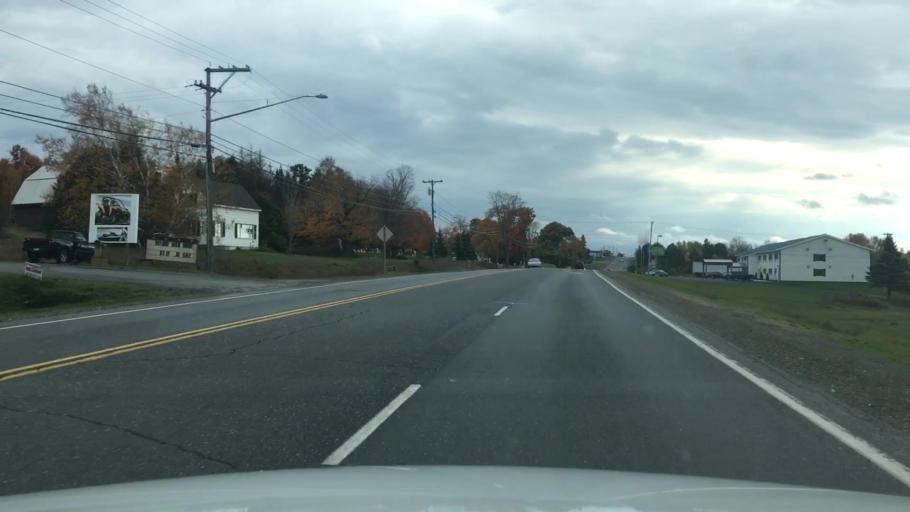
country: US
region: Maine
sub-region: Aroostook County
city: Presque Isle
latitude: 46.6664
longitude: -68.0111
